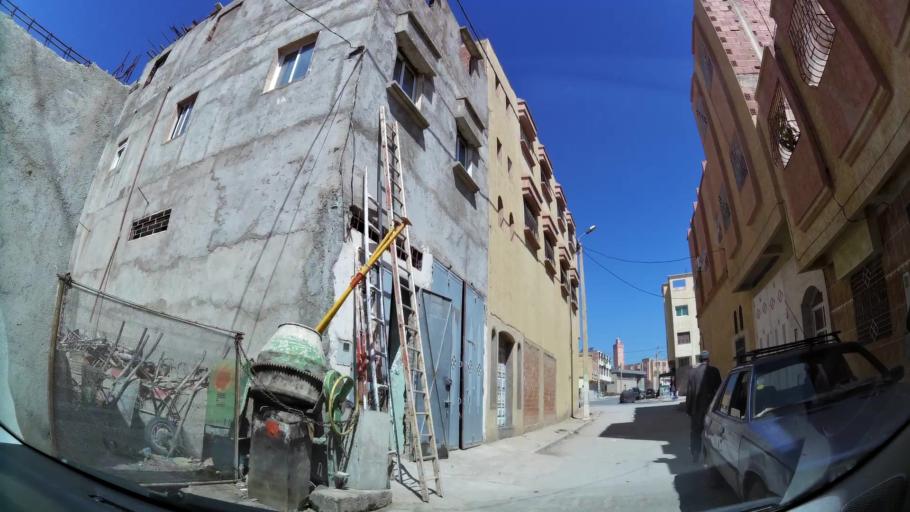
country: MA
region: Oriental
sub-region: Oujda-Angad
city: Oujda
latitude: 34.6695
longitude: -1.9454
